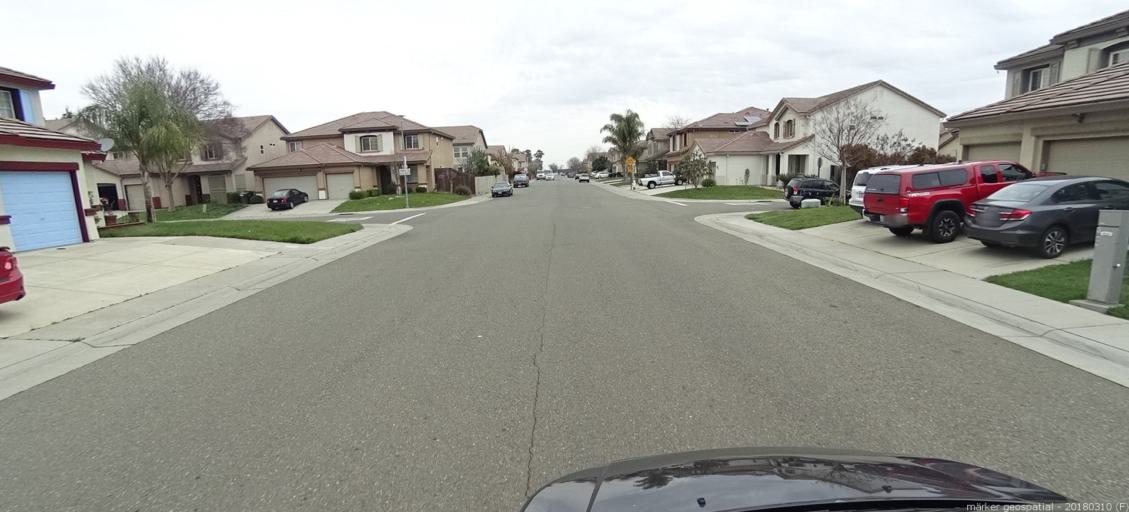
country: US
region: California
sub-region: Sacramento County
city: Vineyard
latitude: 38.4778
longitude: -121.3746
